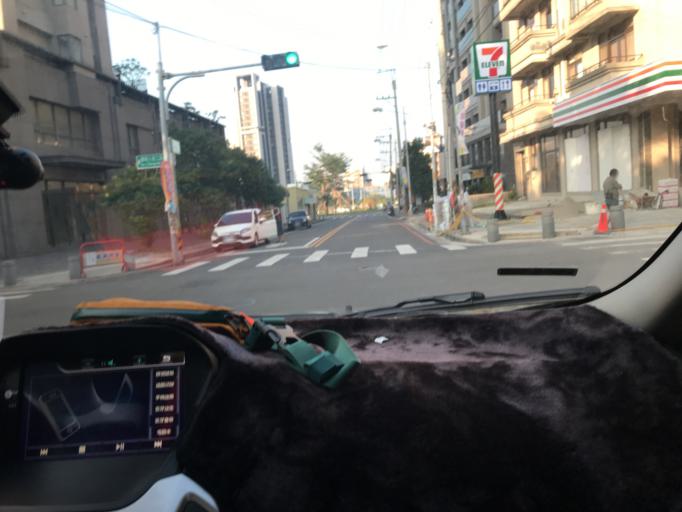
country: TW
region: Taiwan
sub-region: Hsinchu
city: Zhubei
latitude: 24.8227
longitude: 121.0329
